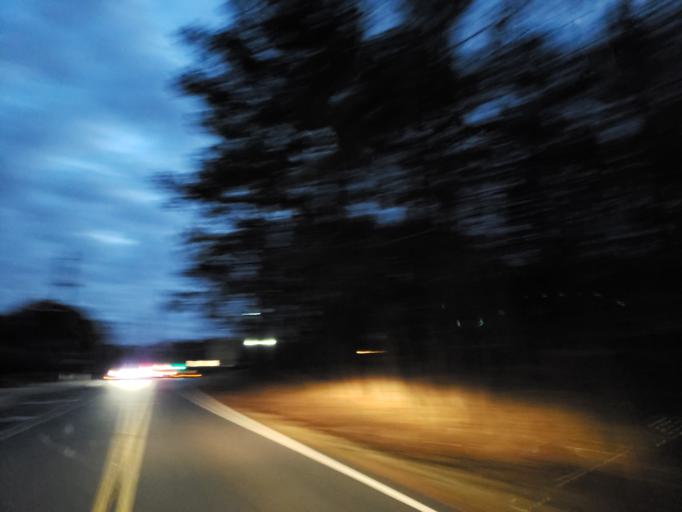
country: US
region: Georgia
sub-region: Cobb County
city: Kennesaw
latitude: 34.0001
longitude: -84.6488
